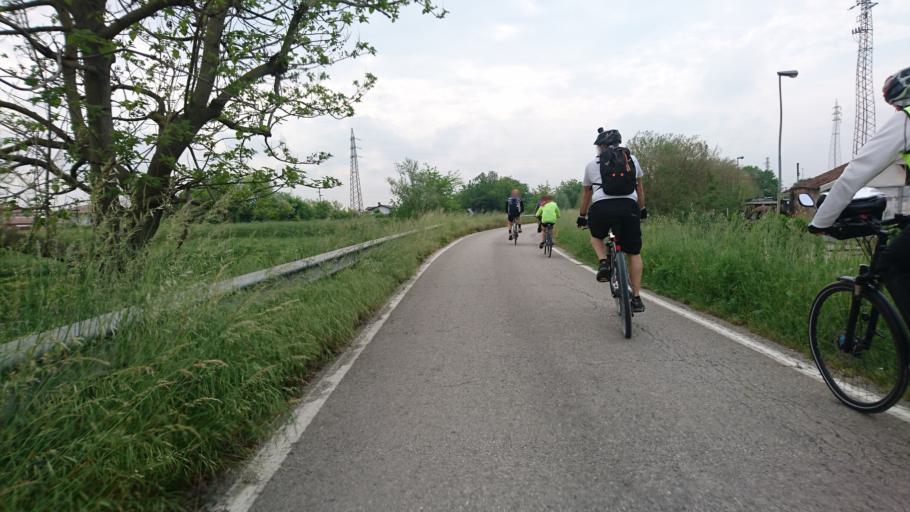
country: IT
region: Veneto
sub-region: Provincia di Padova
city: Battaglia Terme
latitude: 45.2868
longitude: 11.7879
